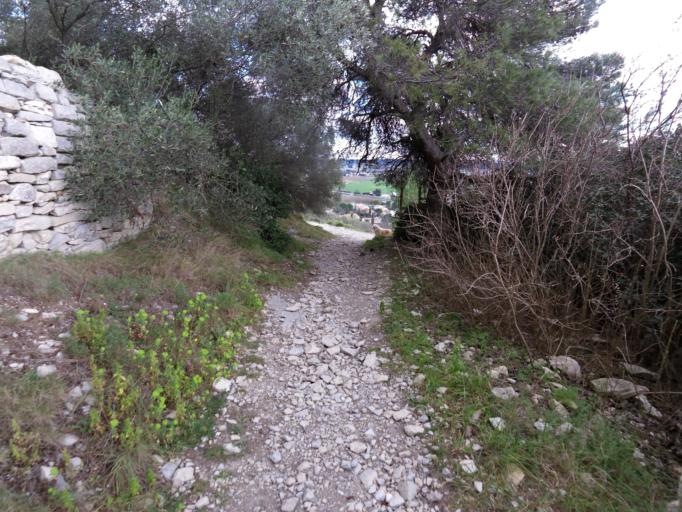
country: FR
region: Languedoc-Roussillon
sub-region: Departement du Gard
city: Calvisson
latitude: 43.7814
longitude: 4.1884
